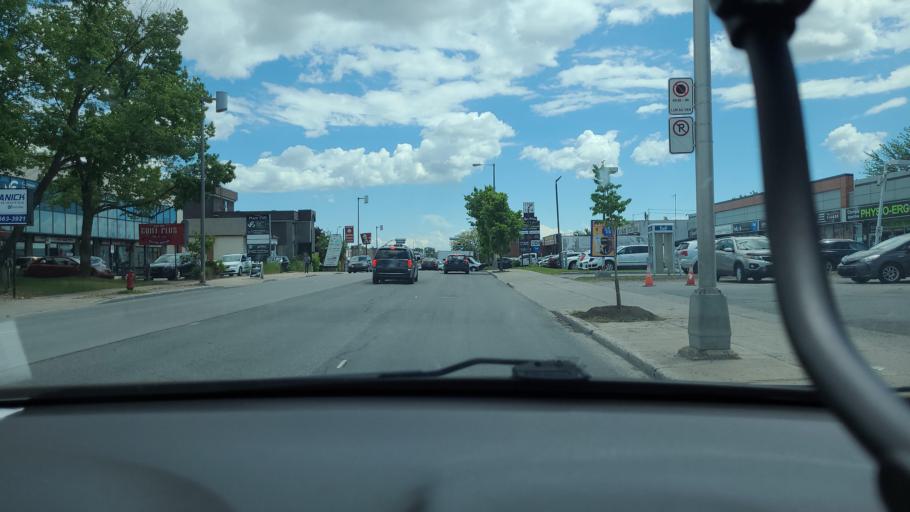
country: CA
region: Quebec
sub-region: Laval
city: Laval
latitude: 45.5976
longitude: -73.7228
